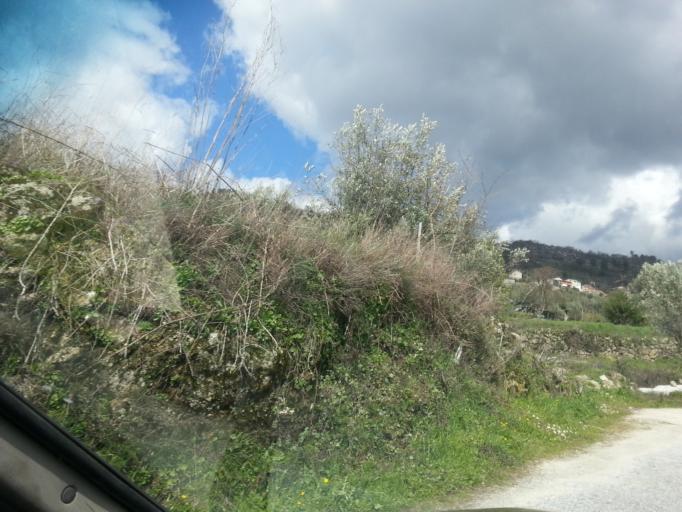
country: PT
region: Guarda
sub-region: Fornos de Algodres
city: Fornos de Algodres
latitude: 40.6590
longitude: -7.4957
